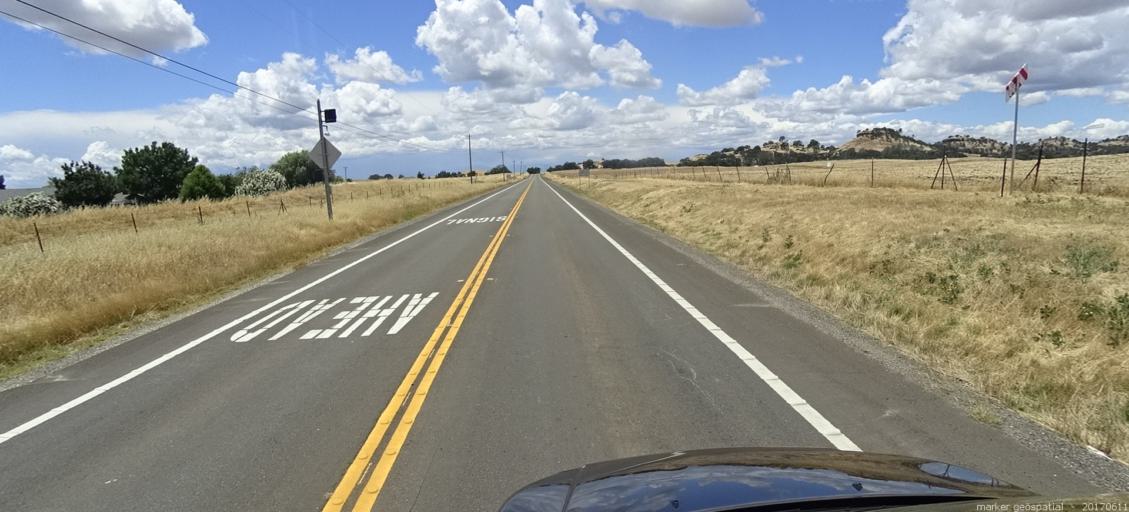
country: US
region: California
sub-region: Butte County
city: Paradise
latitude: 39.6417
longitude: -121.6520
